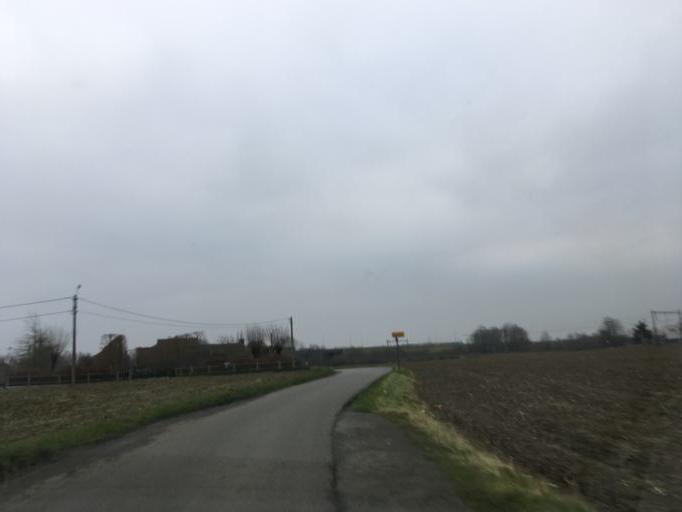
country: BE
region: Flanders
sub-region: Provincie West-Vlaanderen
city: Roeselare
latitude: 50.9836
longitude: 3.1241
